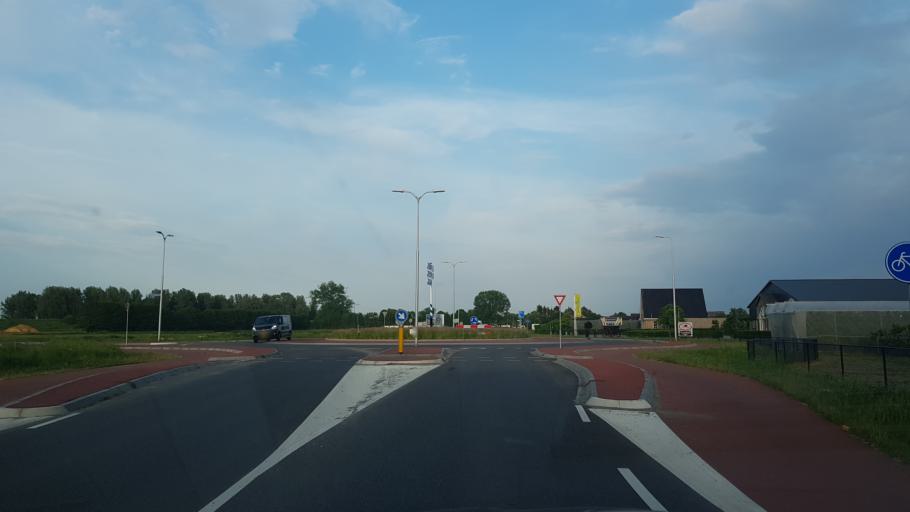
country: NL
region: Gelderland
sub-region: Gemeente Druten
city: Druten
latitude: 51.8863
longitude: 5.6214
